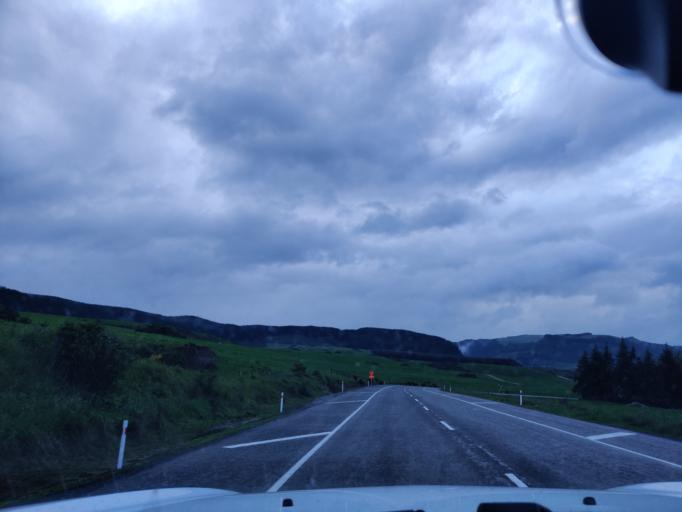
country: NZ
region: Waikato
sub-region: South Waikato District
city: Tokoroa
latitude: -38.4153
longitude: 175.8090
